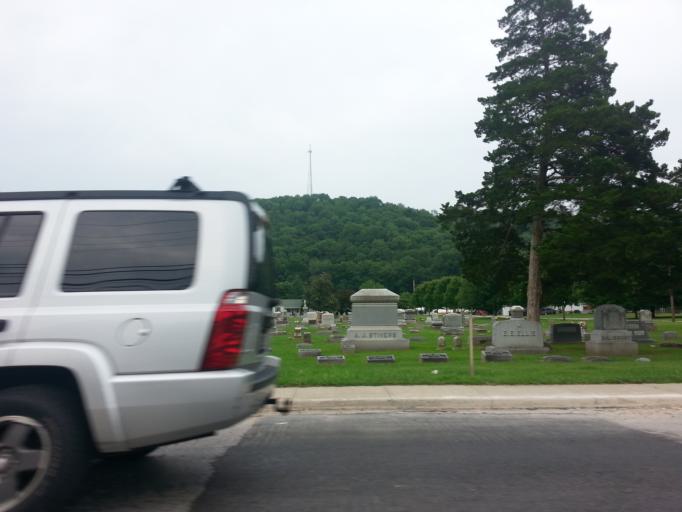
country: US
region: Ohio
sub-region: Brown County
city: Ripley
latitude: 38.7342
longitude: -83.8385
